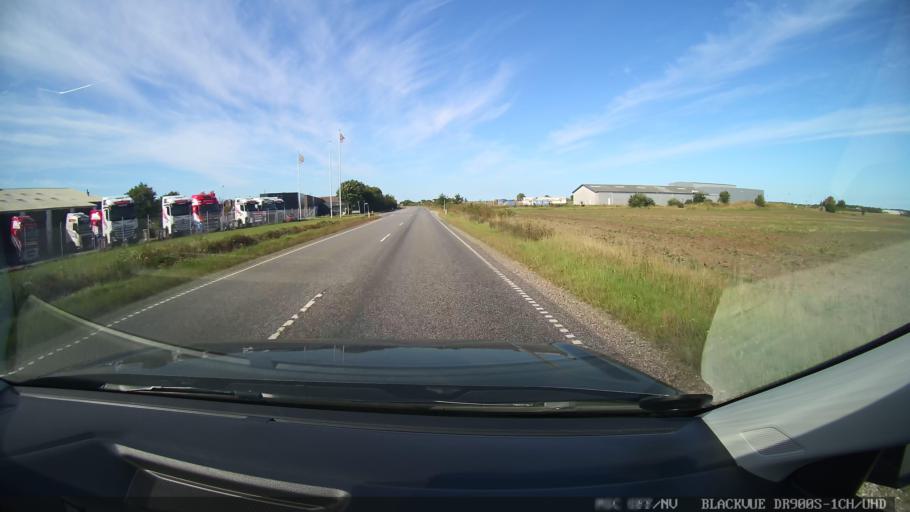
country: DK
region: North Denmark
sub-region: Mariagerfjord Kommune
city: Hobro
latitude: 56.6571
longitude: 9.8118
